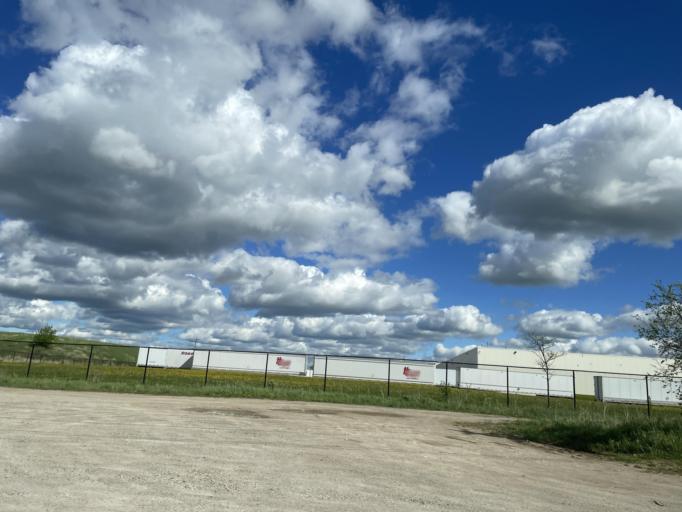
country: CA
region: Ontario
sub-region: Wellington County
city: Guelph
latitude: 43.4916
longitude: -80.2007
